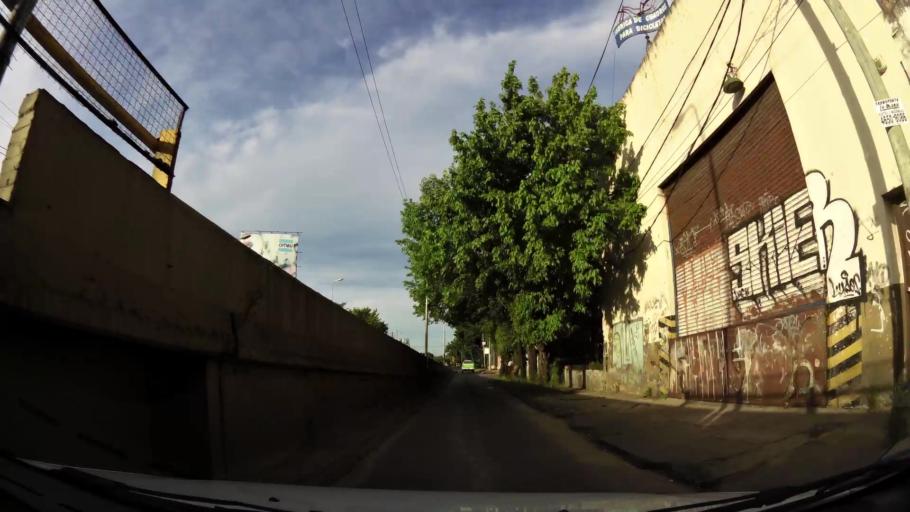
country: AR
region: Buenos Aires
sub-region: Partido de Moron
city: Moron
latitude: -34.6467
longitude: -58.6274
